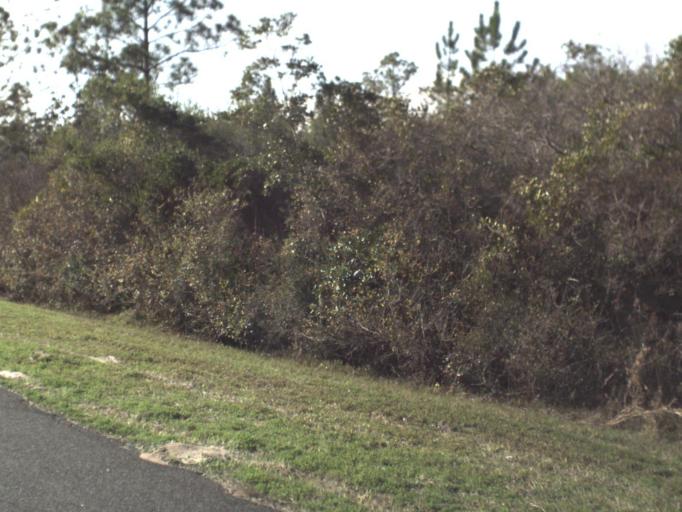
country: US
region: Florida
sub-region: Bay County
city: Youngstown
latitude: 30.4357
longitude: -85.4331
